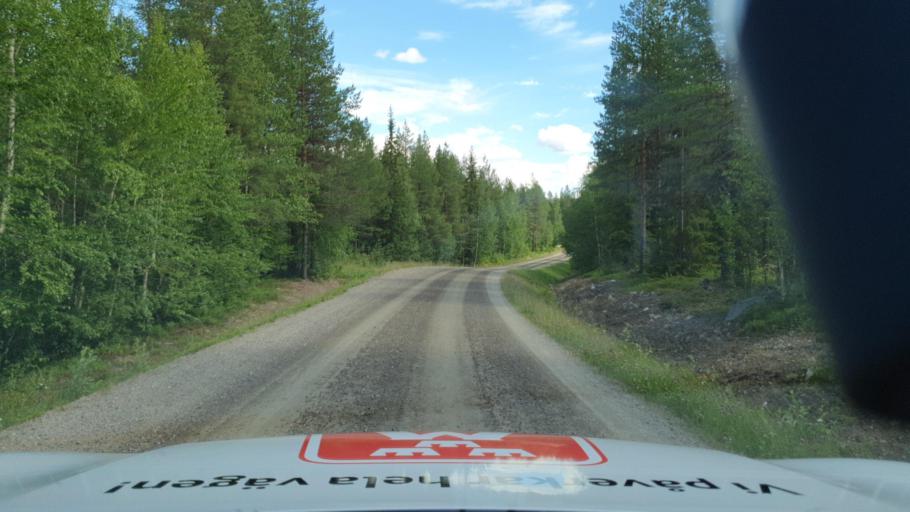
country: SE
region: Vaesterbotten
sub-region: Sorsele Kommun
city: Sorsele
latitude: 65.6716
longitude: 17.2684
